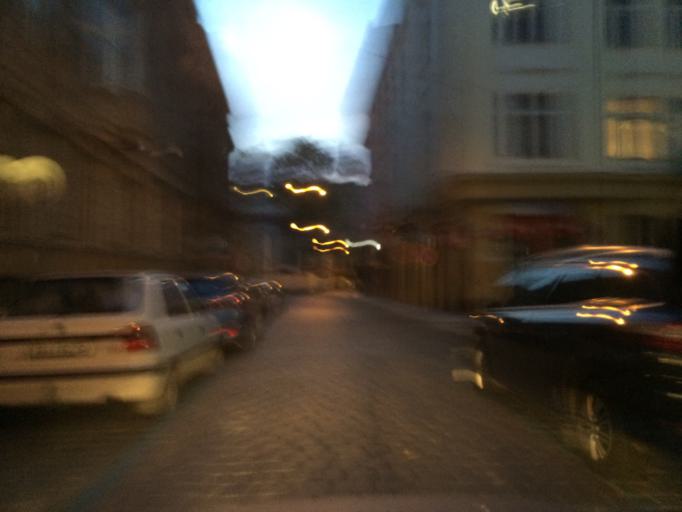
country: CZ
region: Praha
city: Prague
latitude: 50.0836
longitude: 14.4305
